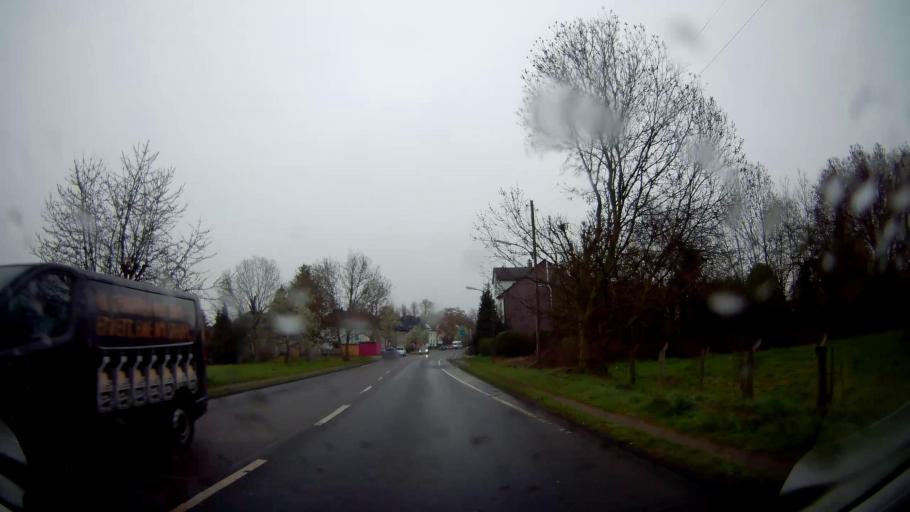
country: DE
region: North Rhine-Westphalia
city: Castrop-Rauxel
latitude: 51.5245
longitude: 7.3122
